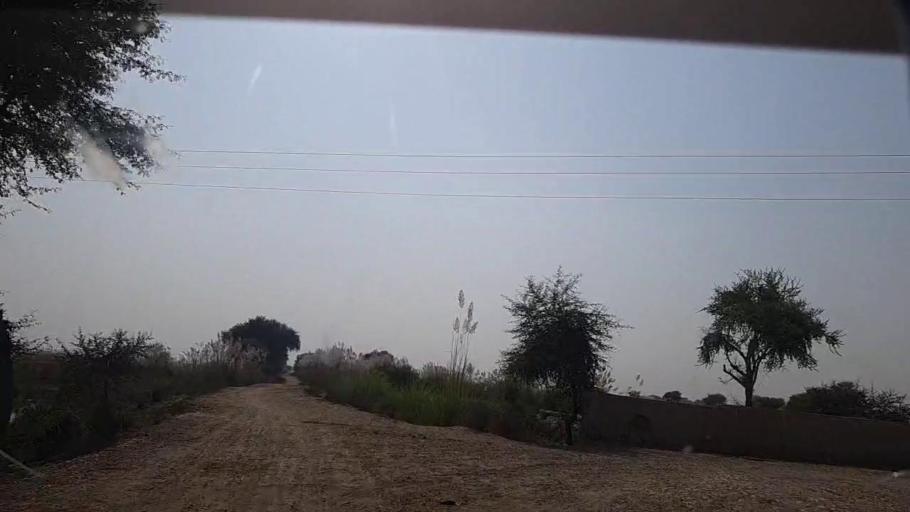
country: PK
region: Sindh
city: Shikarpur
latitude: 28.1150
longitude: 68.6582
